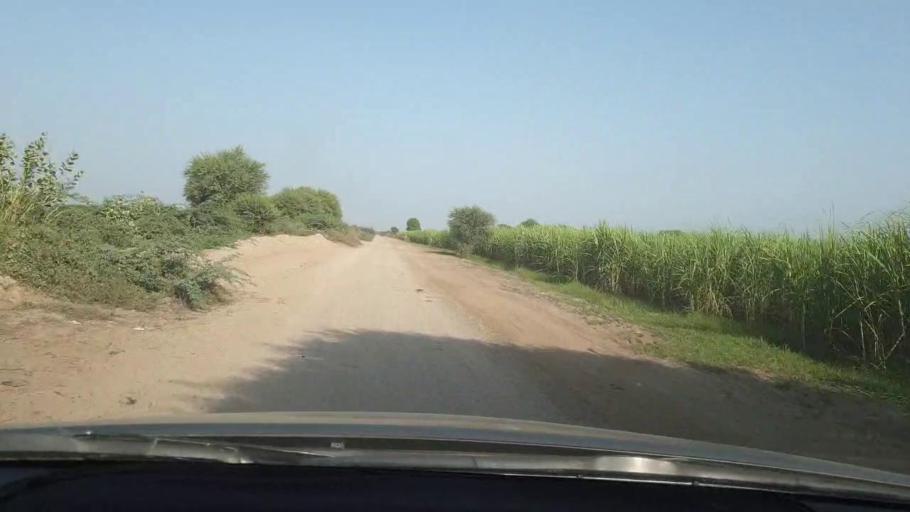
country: PK
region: Sindh
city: Naukot
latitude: 24.7781
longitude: 69.2701
